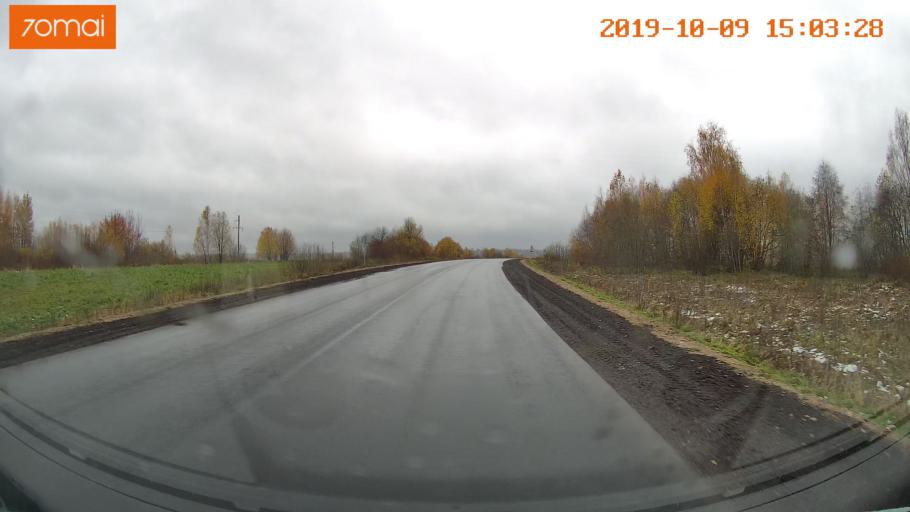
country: RU
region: Kostroma
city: Chistyye Bory
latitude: 58.2708
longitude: 41.6755
